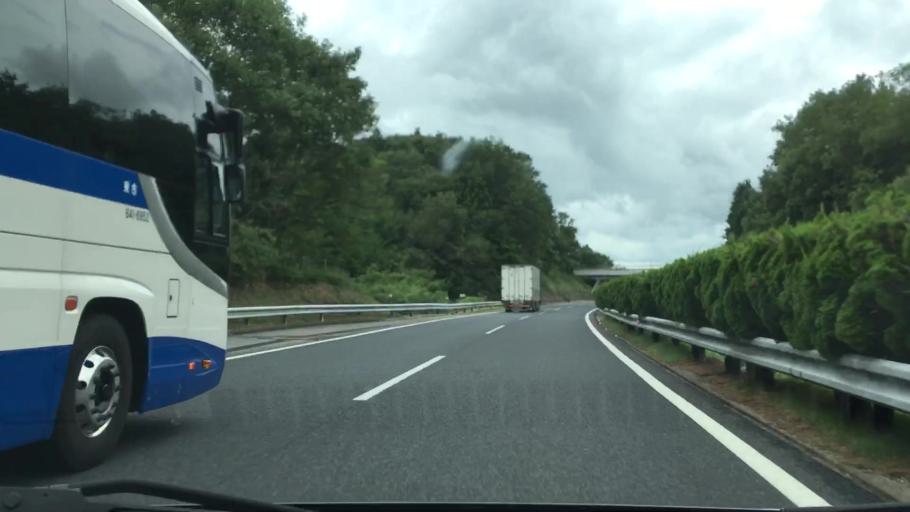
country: JP
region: Okayama
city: Tsuyama
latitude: 35.0359
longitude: 134.1346
